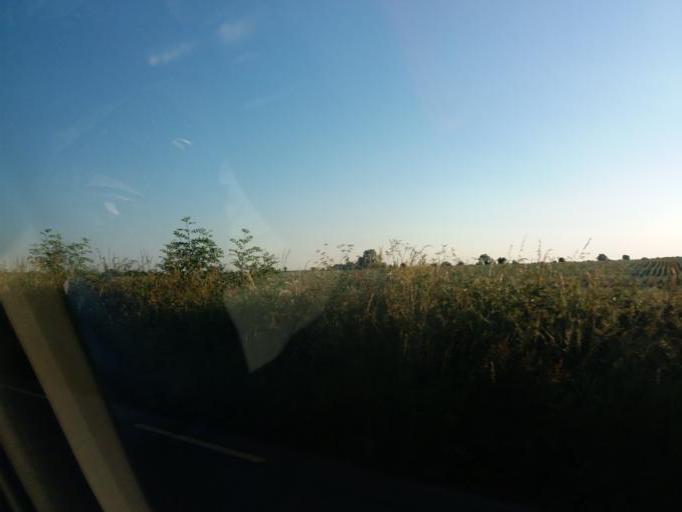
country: IE
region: Leinster
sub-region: An Mhi
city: Ashbourne
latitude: 53.5256
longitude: -6.3596
